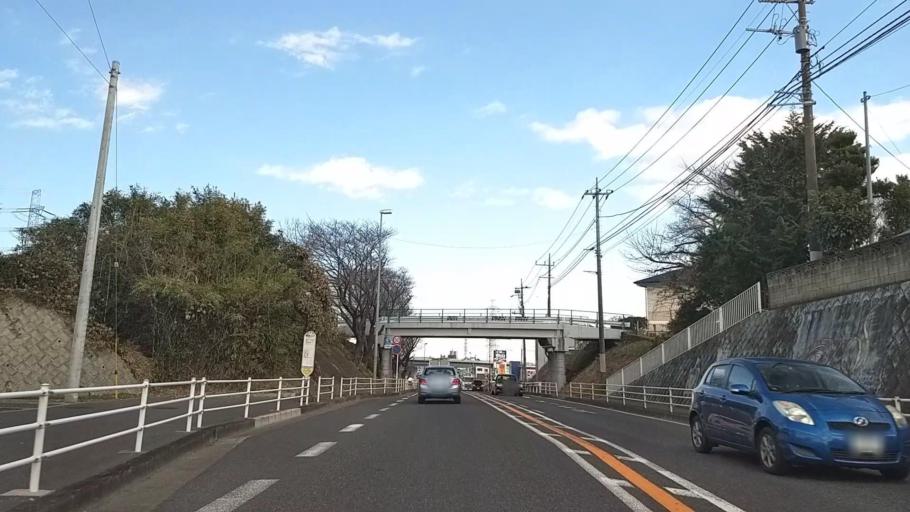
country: JP
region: Kanagawa
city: Isehara
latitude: 35.4065
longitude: 139.3191
